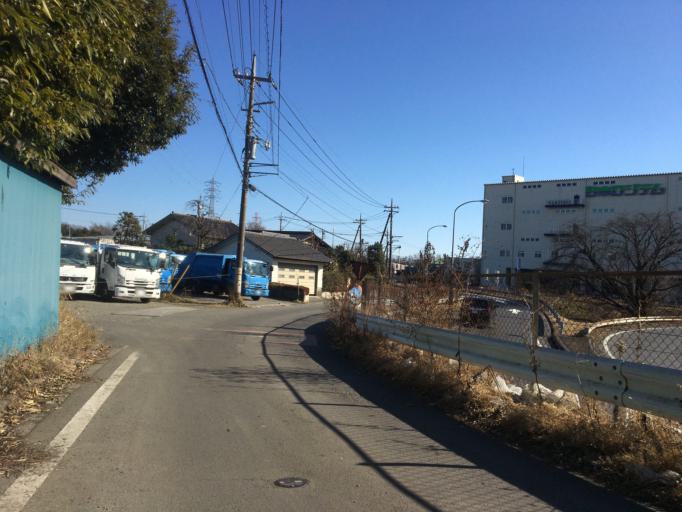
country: JP
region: Saitama
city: Oi
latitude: 35.8115
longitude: 139.5345
